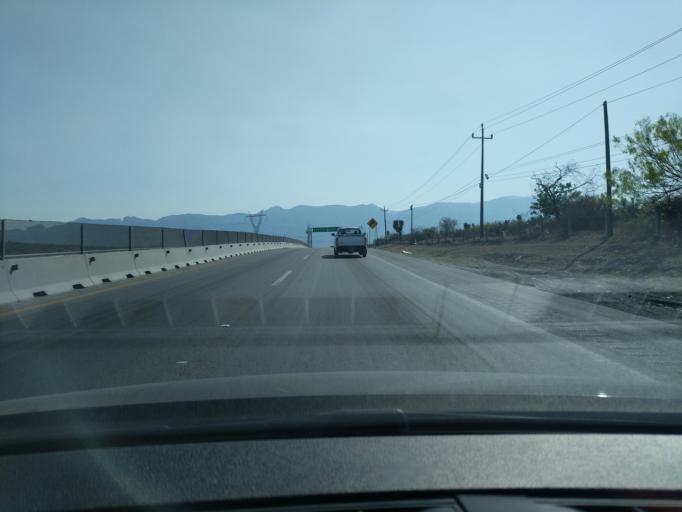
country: MX
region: Nuevo Leon
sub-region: Garcia
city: Los Parques
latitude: 25.7474
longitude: -100.5111
